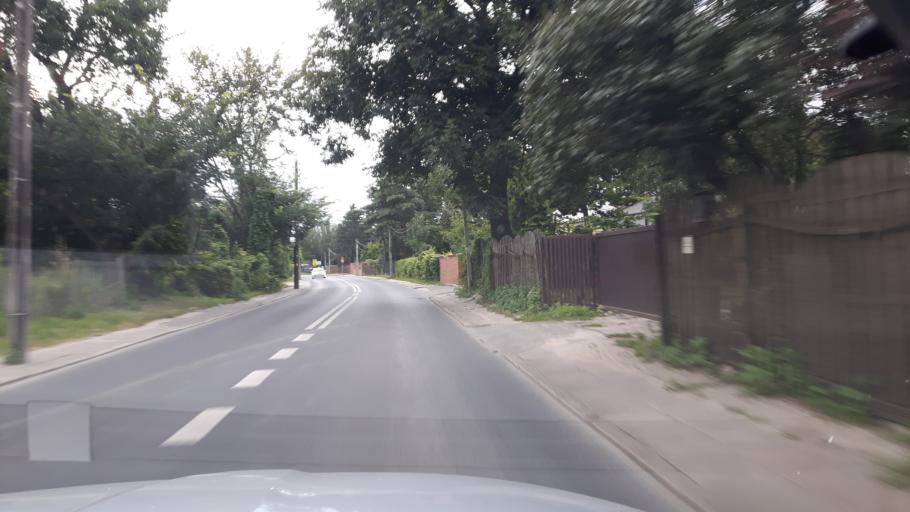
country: PL
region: Masovian Voivodeship
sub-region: Warszawa
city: Praga Poludnie
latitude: 52.2103
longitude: 21.0756
